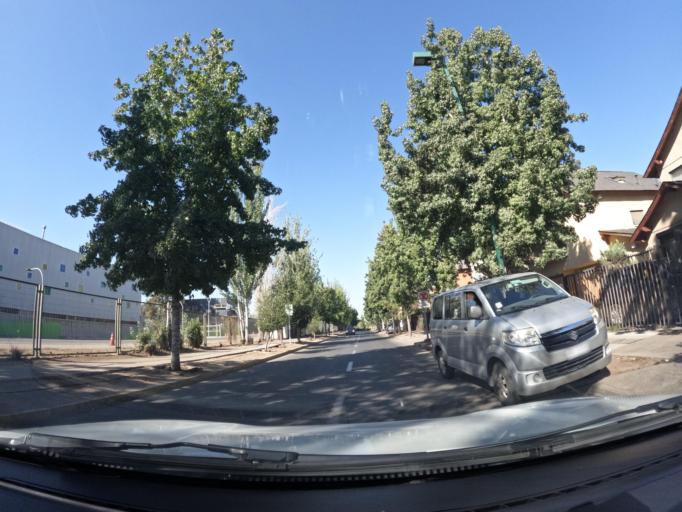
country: CL
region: Santiago Metropolitan
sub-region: Provincia de Santiago
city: Villa Presidente Frei, Nunoa, Santiago, Chile
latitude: -33.4917
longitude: -70.5771
